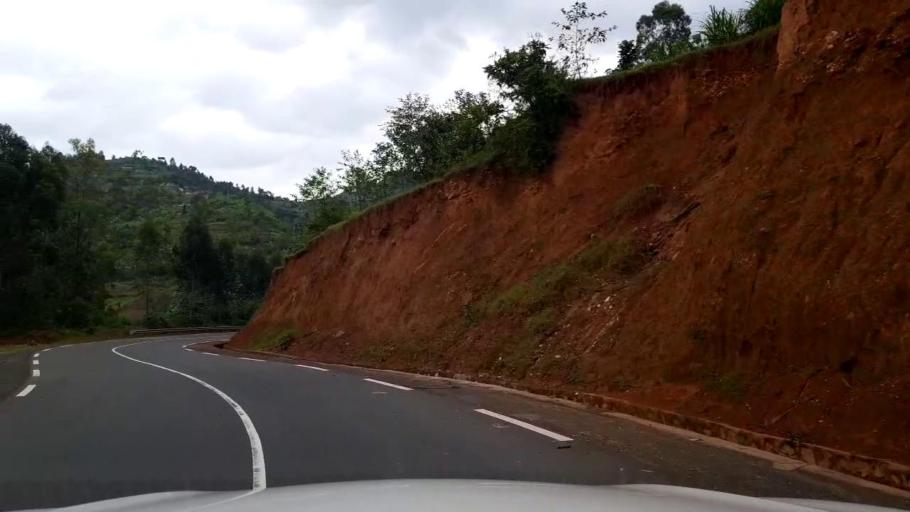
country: RW
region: Western Province
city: Kibuye
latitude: -1.9062
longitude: 29.3641
